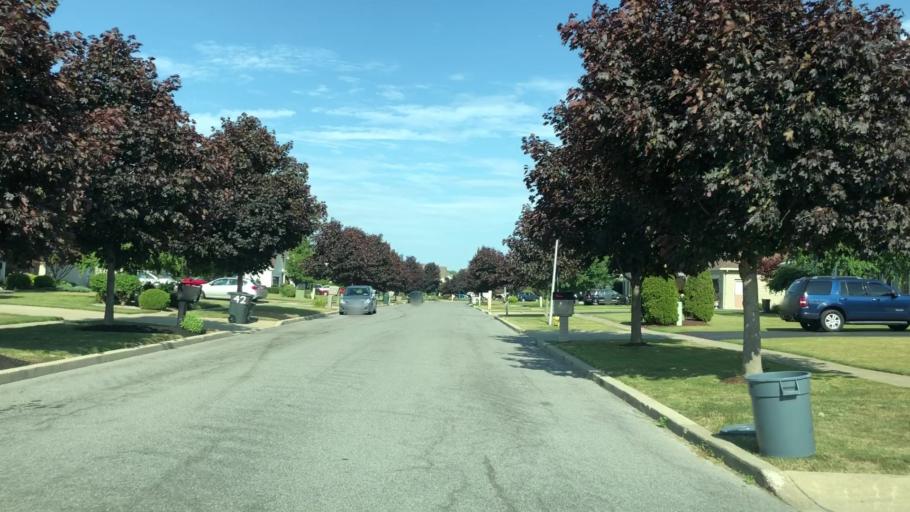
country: US
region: New York
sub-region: Erie County
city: Lancaster
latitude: 42.8767
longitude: -78.6838
